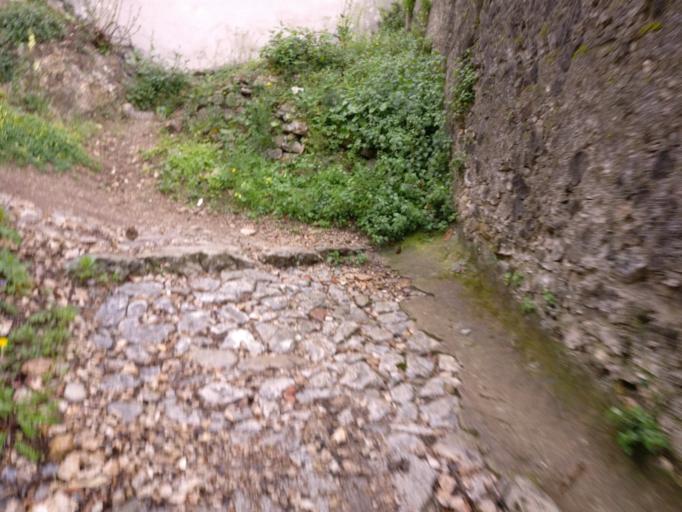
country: FR
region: Provence-Alpes-Cote d'Azur
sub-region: Departement des Alpes-Maritimes
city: Villefranche-sur-Mer
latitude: 43.7141
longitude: 7.2978
